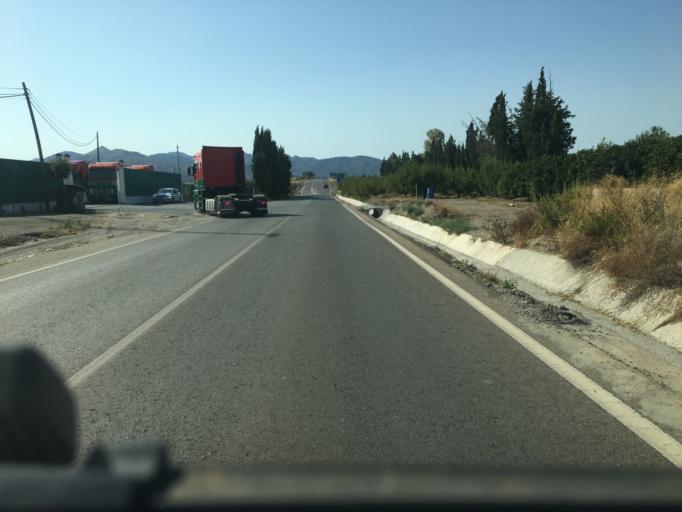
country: ES
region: Andalusia
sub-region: Provincia de Almeria
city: Huercal-Overa
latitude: 37.4106
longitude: -1.9614
